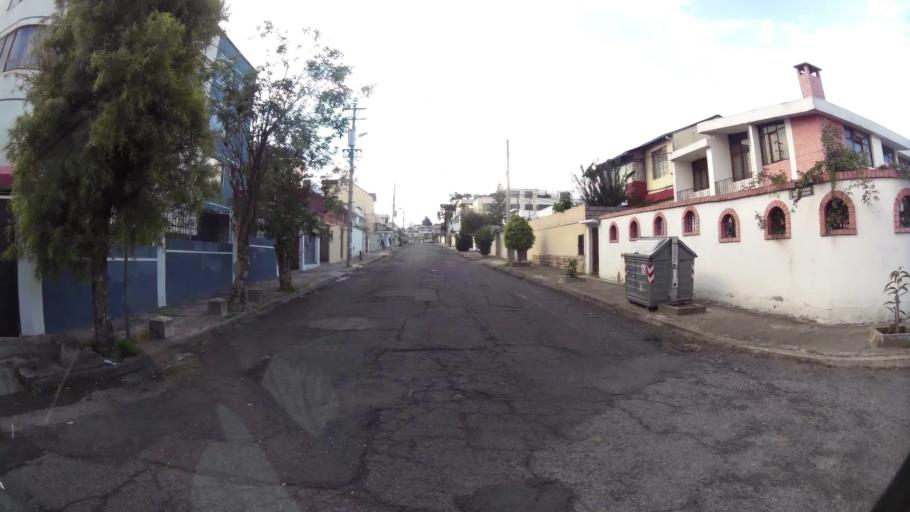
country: EC
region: Pichincha
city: Quito
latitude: -0.1341
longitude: -78.4792
